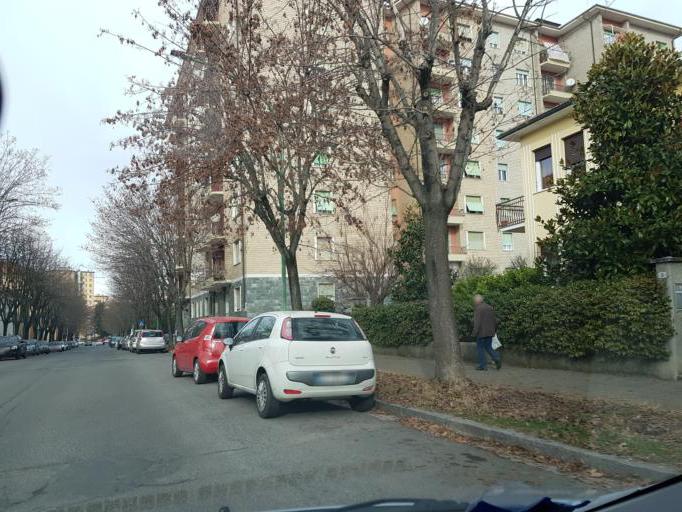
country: IT
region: Piedmont
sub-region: Provincia di Alessandria
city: Novi Ligure
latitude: 44.7612
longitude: 8.7973
